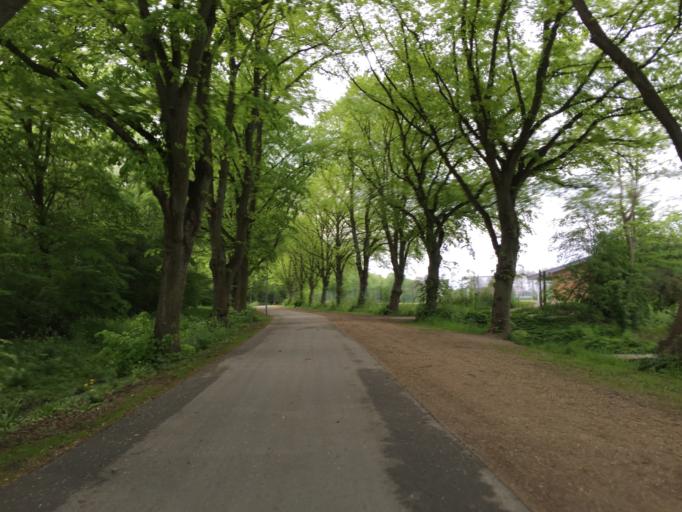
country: DK
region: Capital Region
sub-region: Brondby Kommune
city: Brondbyvester
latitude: 55.6272
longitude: 12.4409
